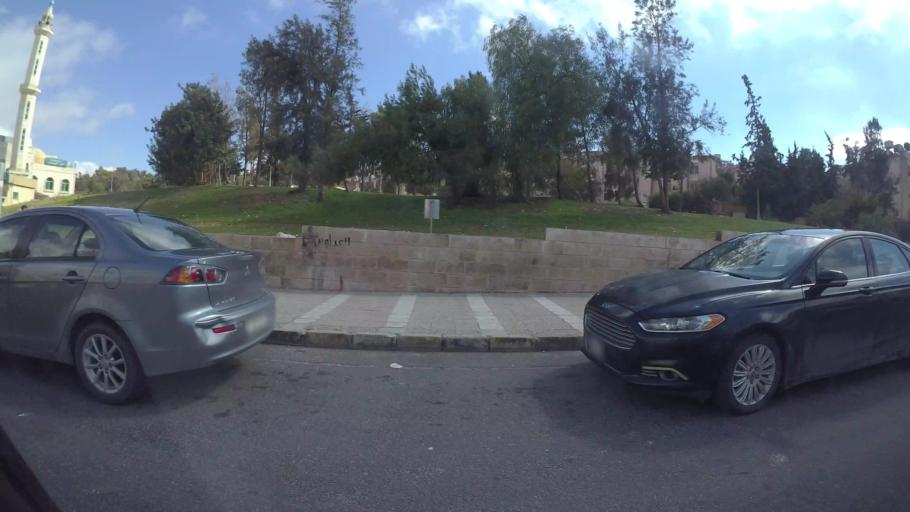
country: JO
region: Amman
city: Al Jubayhah
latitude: 32.0591
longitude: 35.8767
